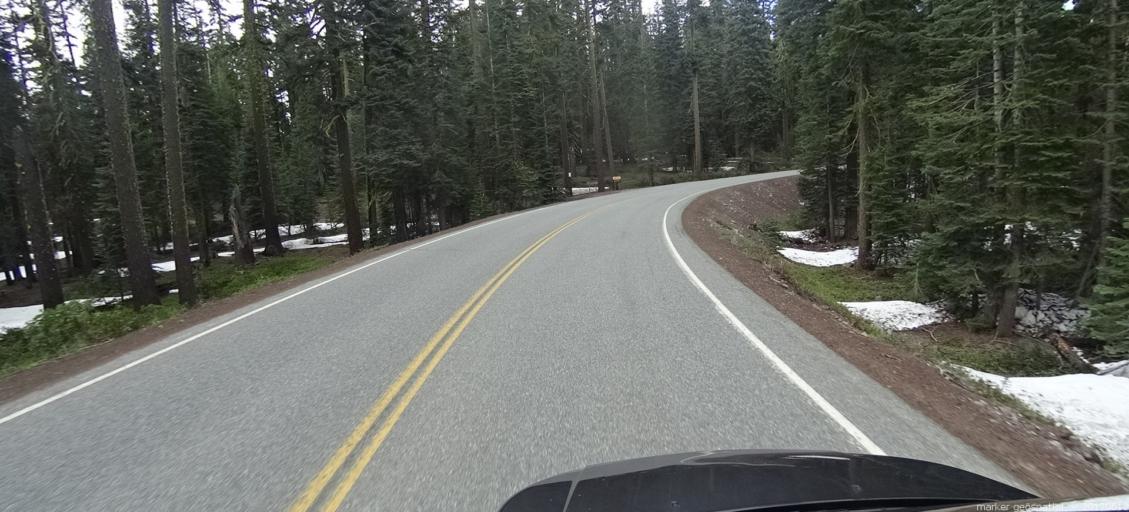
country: US
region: California
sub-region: Siskiyou County
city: Mount Shasta
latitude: 41.3445
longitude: -122.2532
